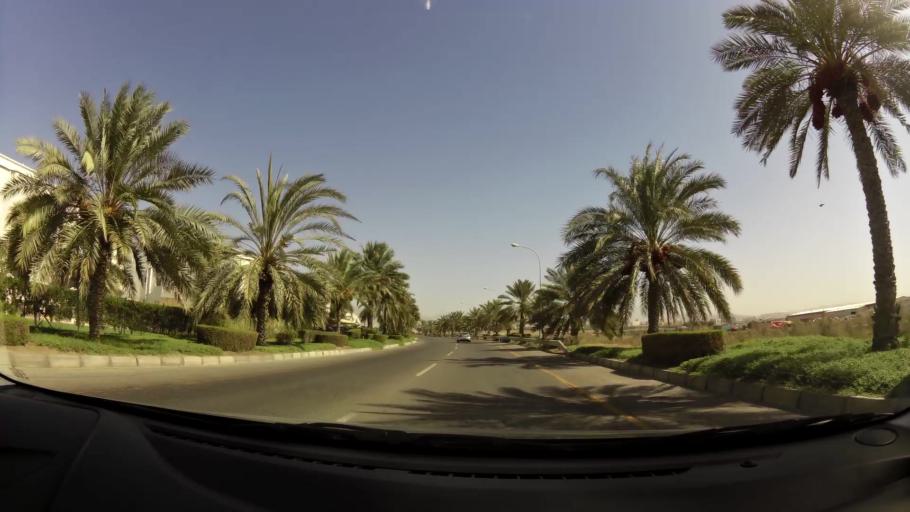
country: OM
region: Muhafazat Masqat
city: Bawshar
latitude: 23.5989
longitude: 58.3471
